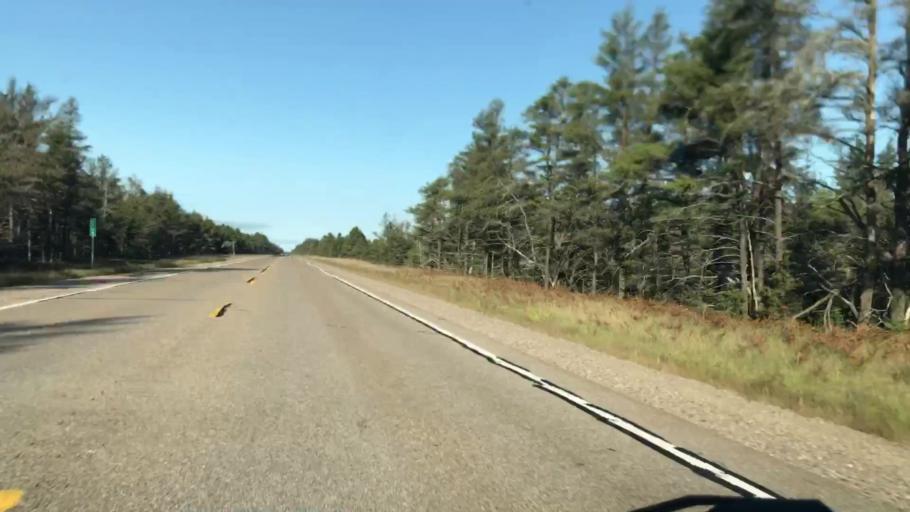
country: US
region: Michigan
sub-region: Chippewa County
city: Sault Ste. Marie
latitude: 46.3587
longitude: -84.8221
